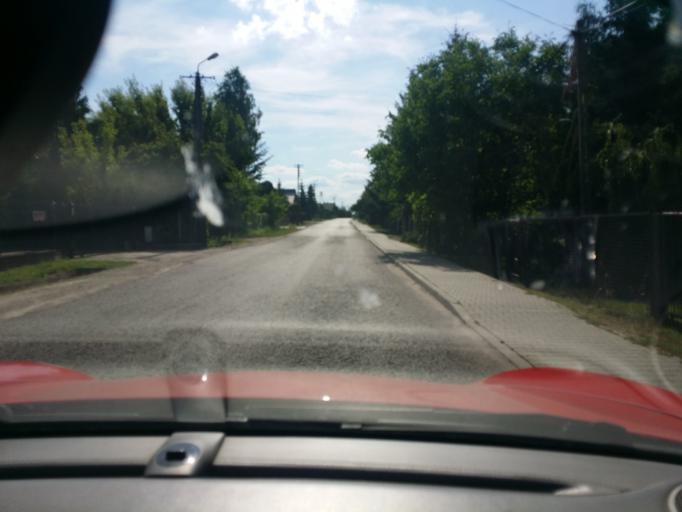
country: PL
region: Masovian Voivodeship
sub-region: Powiat radomski
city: Trablice
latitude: 51.3489
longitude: 21.1076
